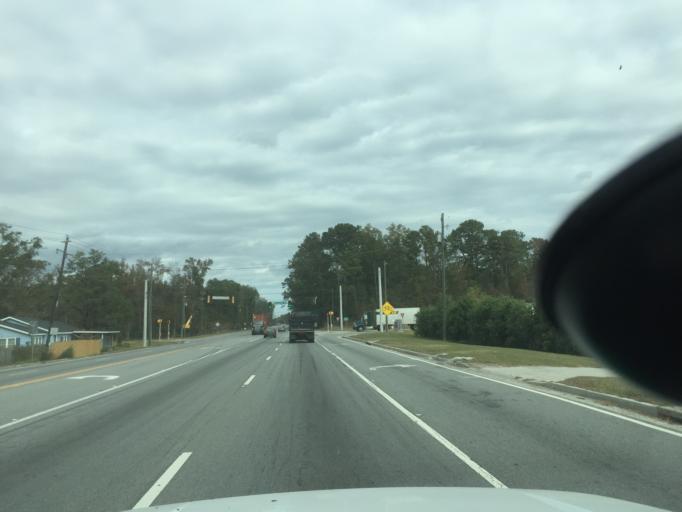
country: US
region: Georgia
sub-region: Chatham County
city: Garden City
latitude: 32.0958
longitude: -81.1964
